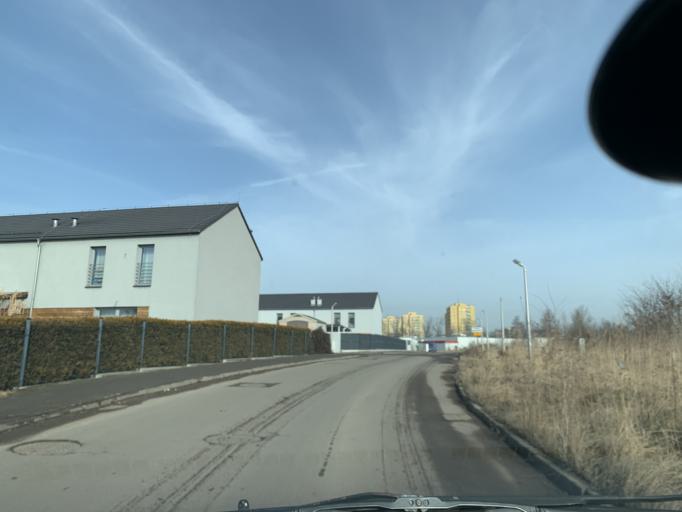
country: PL
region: Silesian Voivodeship
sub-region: Bytom
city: Bytom
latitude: 50.3362
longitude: 18.9047
